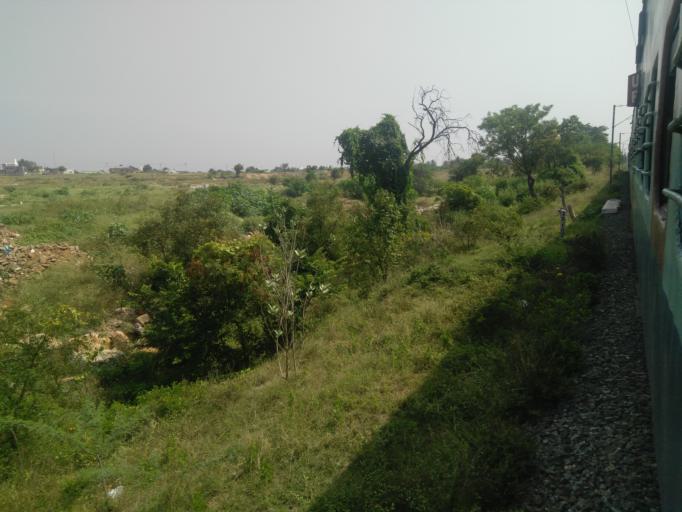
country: IN
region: Tamil Nadu
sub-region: Coimbatore
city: Mettupalayam
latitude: 11.2758
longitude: 76.9432
